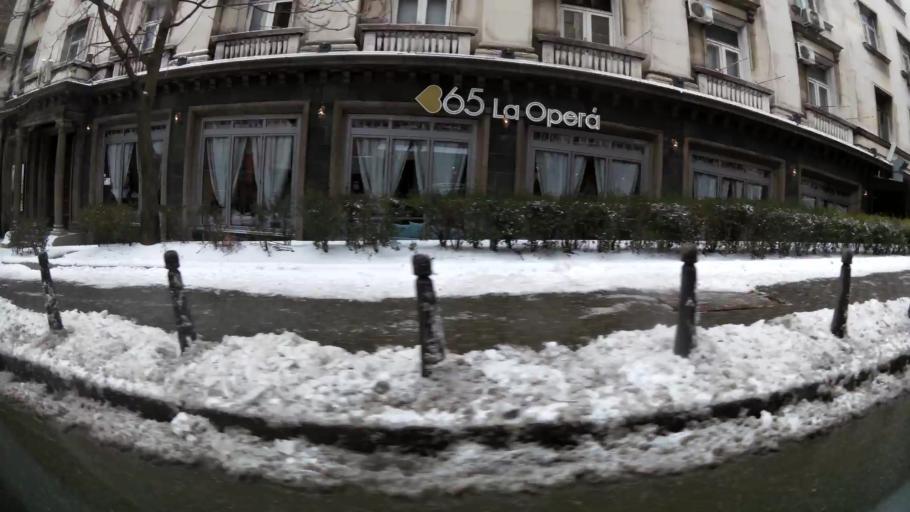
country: BG
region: Sofia-Capital
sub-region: Stolichna Obshtina
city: Sofia
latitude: 42.6977
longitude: 23.3302
